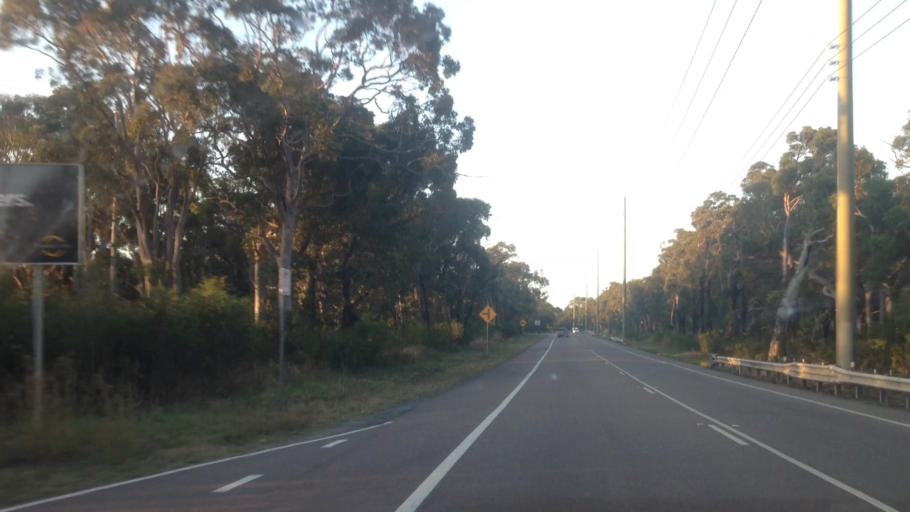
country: AU
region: New South Wales
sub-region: Wyong Shire
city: Kingfisher Shores
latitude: -33.1823
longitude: 151.5383
